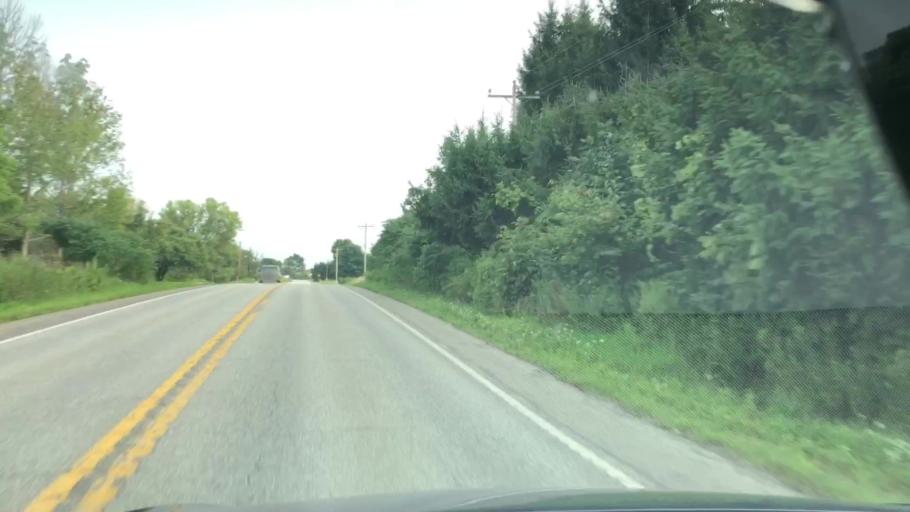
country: US
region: Pennsylvania
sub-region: Erie County
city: Union City
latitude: 41.8761
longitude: -79.8416
